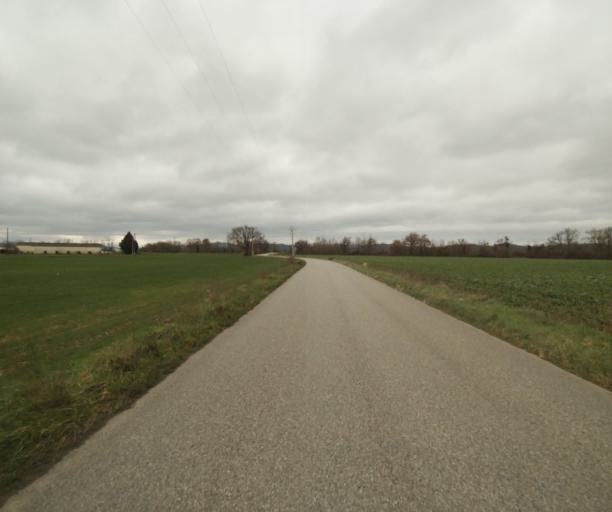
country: FR
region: Midi-Pyrenees
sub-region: Departement de l'Ariege
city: Pamiers
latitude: 43.1433
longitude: 1.6332
